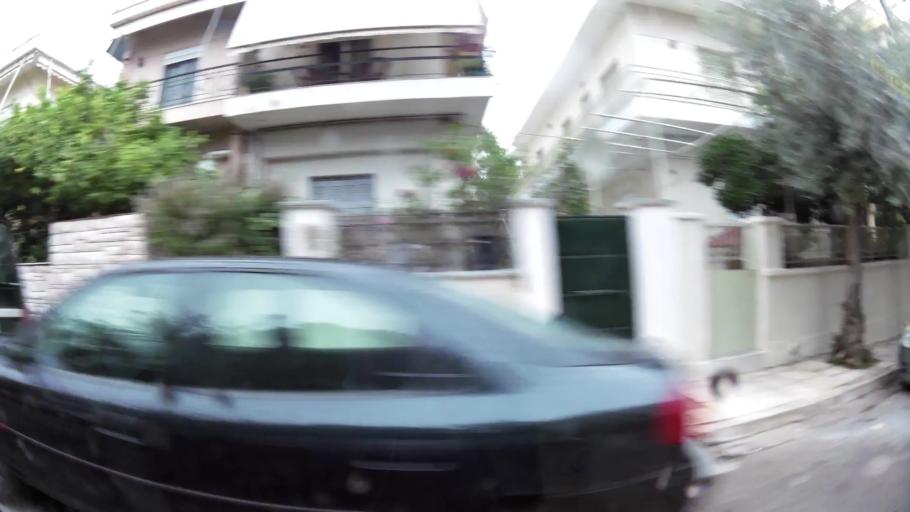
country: GR
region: Attica
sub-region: Nomarchia Athinas
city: Agia Varvara
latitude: 37.9899
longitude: 23.6643
